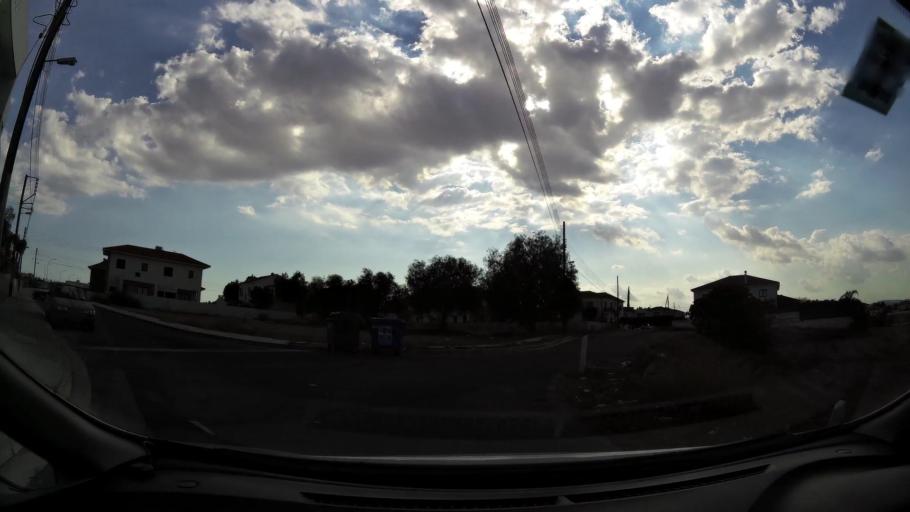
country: CY
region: Larnaka
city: Livadia
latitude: 34.9427
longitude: 33.6112
